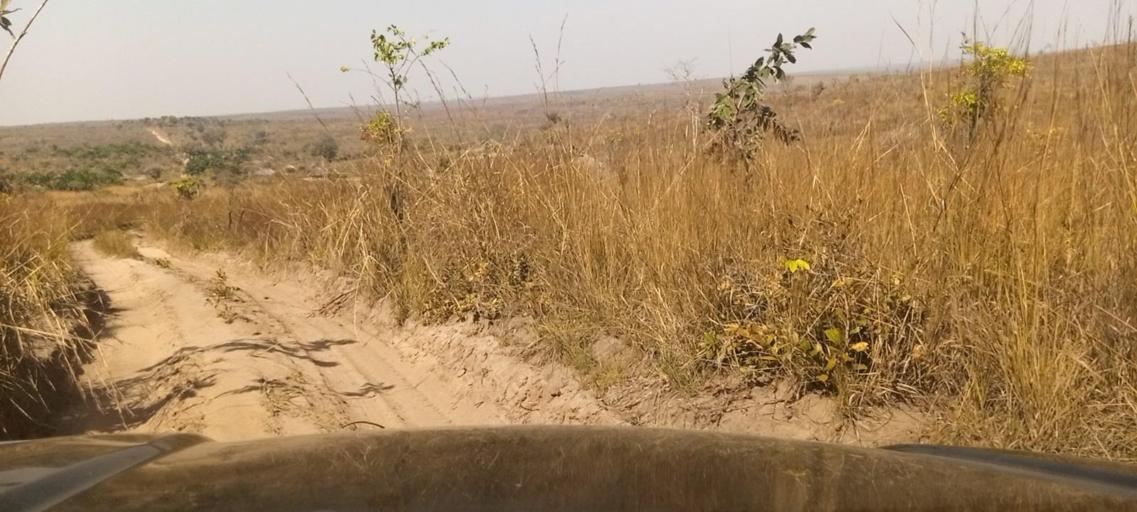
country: CD
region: Kasai-Oriental
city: Kabinda
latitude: -5.7809
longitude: 25.0551
